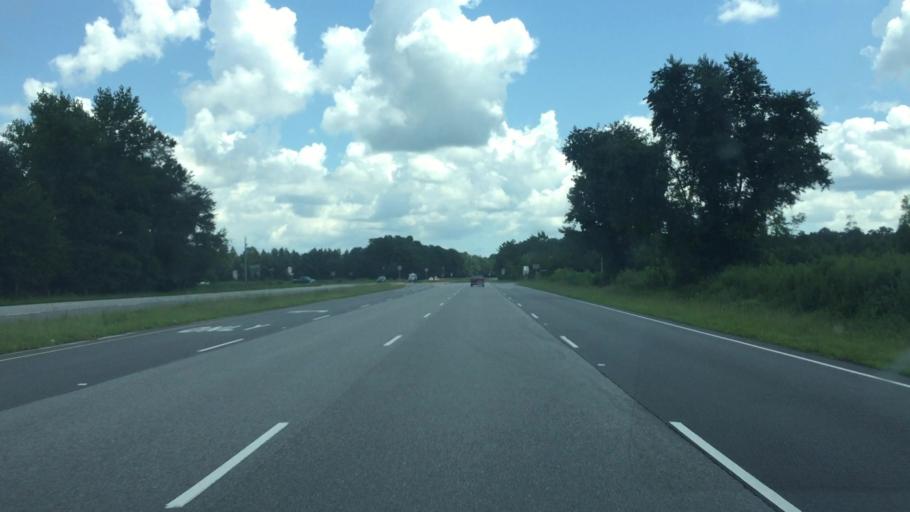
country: US
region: South Carolina
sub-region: Horry County
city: Loris
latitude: 34.0352
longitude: -78.8110
